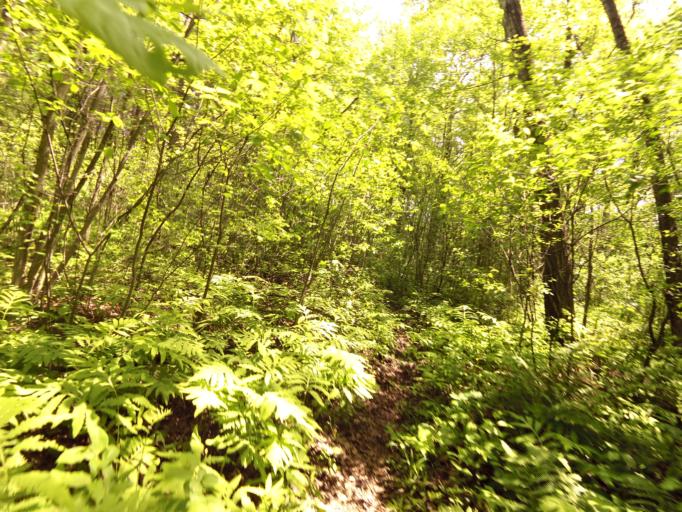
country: CA
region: Ontario
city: Ottawa
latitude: 45.3552
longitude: -75.5942
